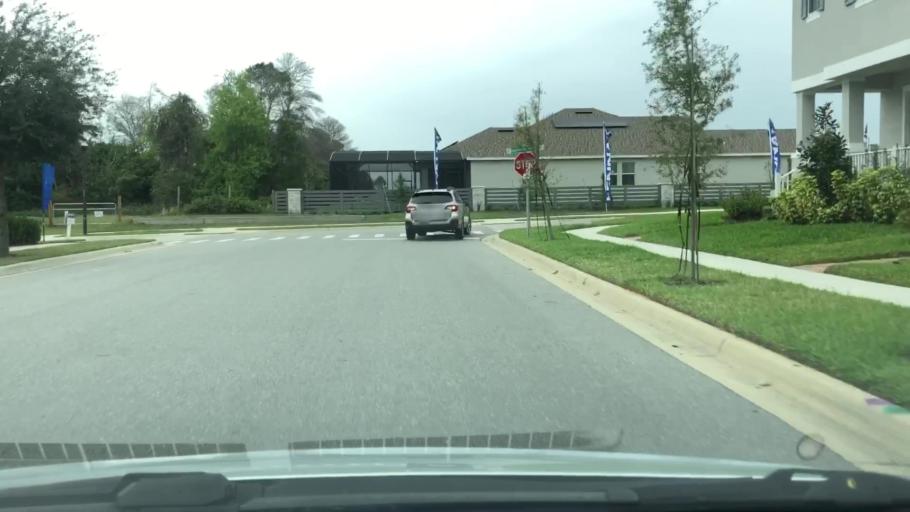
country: US
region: Florida
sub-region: Polk County
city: Citrus Ridge
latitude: 28.4309
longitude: -81.6233
